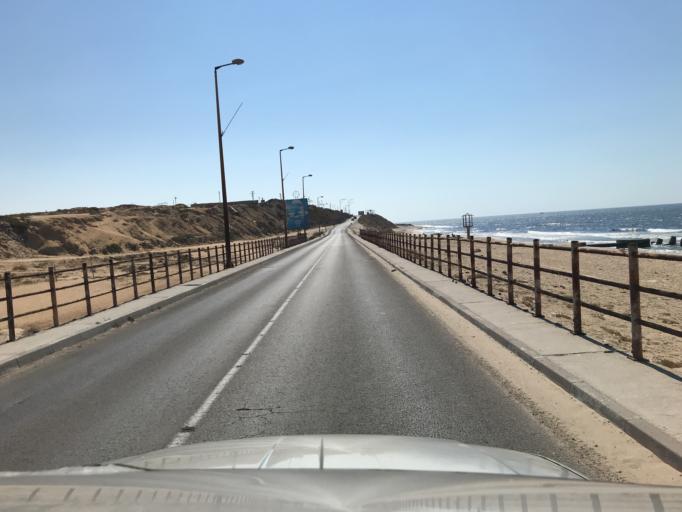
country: PS
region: Gaza Strip
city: An Nusayrat
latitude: 31.4632
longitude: 34.3755
